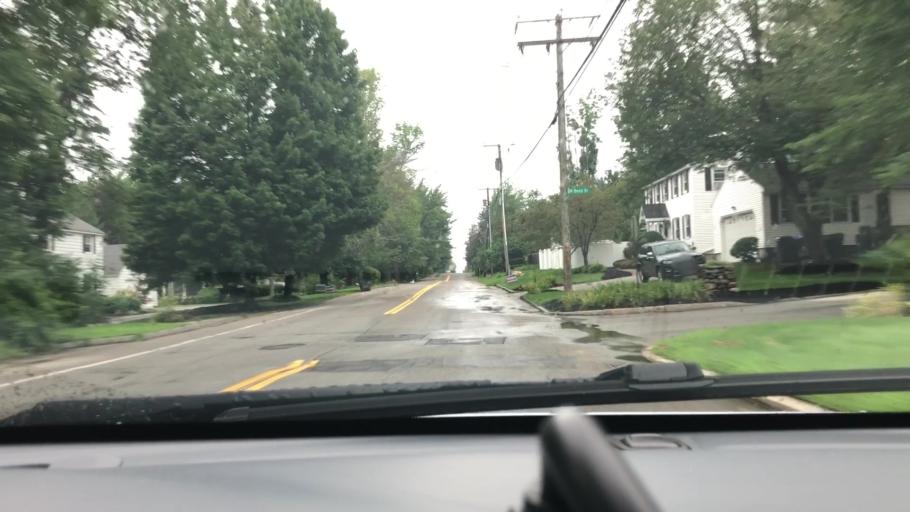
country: US
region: New Hampshire
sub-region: Merrimack County
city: South Hooksett
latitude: 43.0259
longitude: -71.4625
